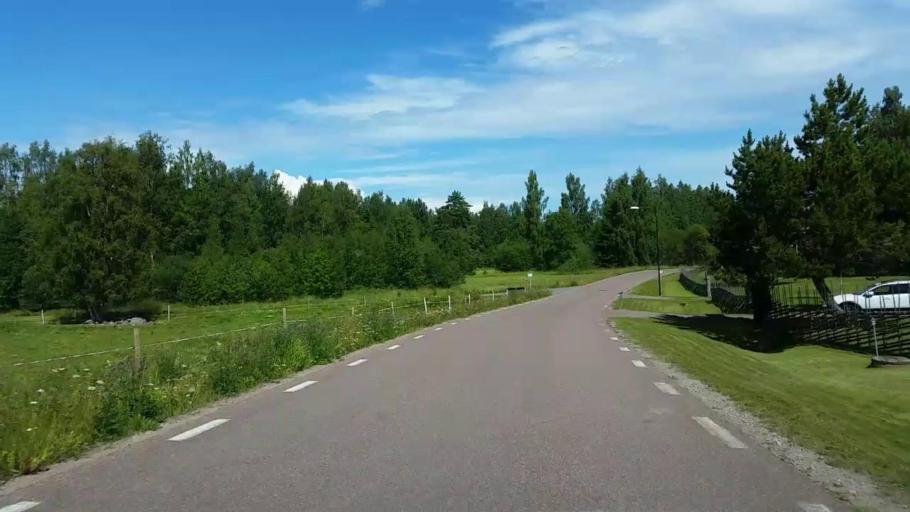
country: SE
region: Dalarna
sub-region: Rattviks Kommun
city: Vikarbyn
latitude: 60.8335
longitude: 14.9931
